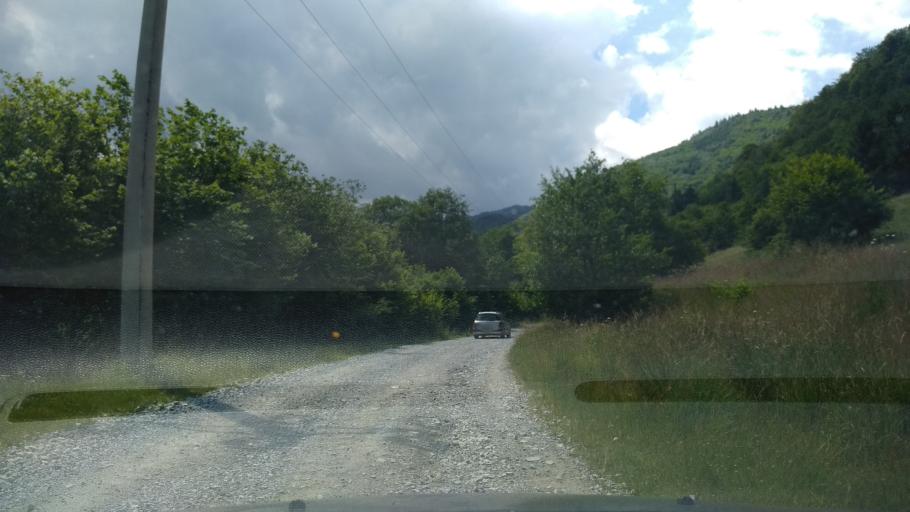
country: RO
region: Hunedoara
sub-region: Comuna Rau de Mori
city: Rau de Mori
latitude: 45.4458
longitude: 22.8941
